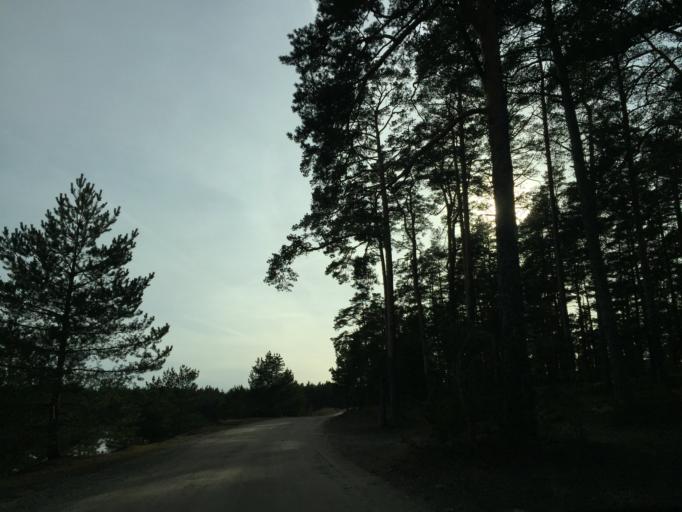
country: EE
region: Paernumaa
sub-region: Paernu linn
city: Parnu
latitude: 58.2139
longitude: 24.5023
